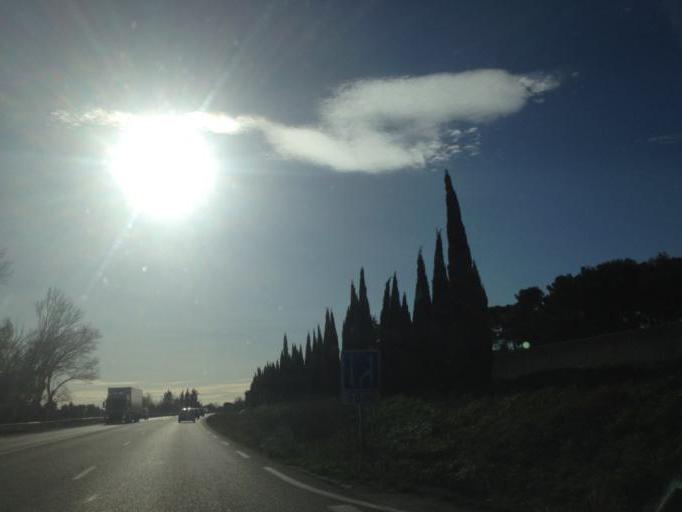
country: FR
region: Provence-Alpes-Cote d'Azur
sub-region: Departement du Vaucluse
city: Courthezon
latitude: 44.0647
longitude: 4.8868
